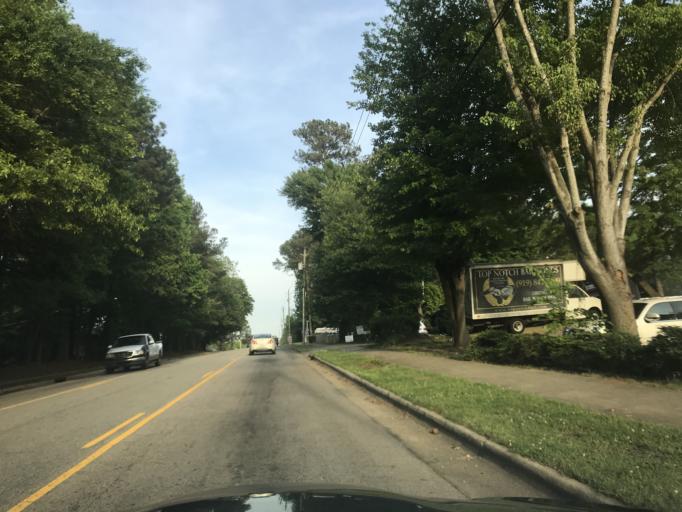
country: US
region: North Carolina
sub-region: Wake County
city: Raleigh
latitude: 35.7417
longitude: -78.6361
